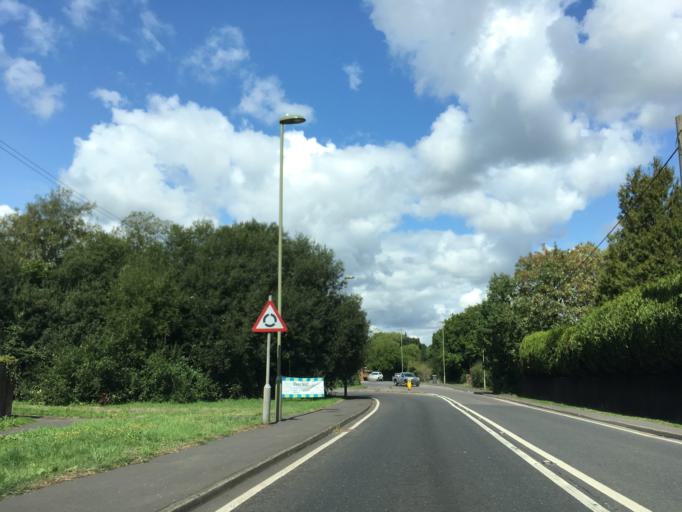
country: GB
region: England
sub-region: Hampshire
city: Colden Common
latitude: 50.9919
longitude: -1.3095
